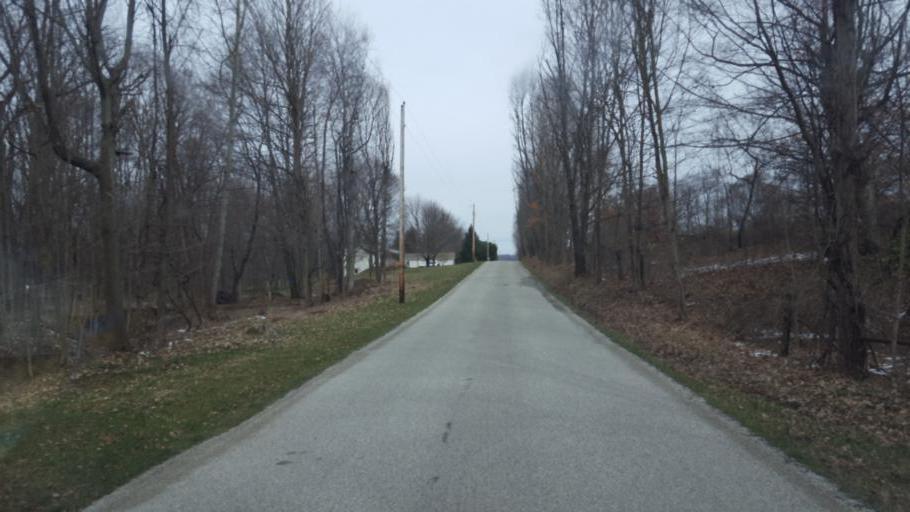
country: US
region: Ohio
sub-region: Sandusky County
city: Bellville
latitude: 40.6014
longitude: -82.5679
